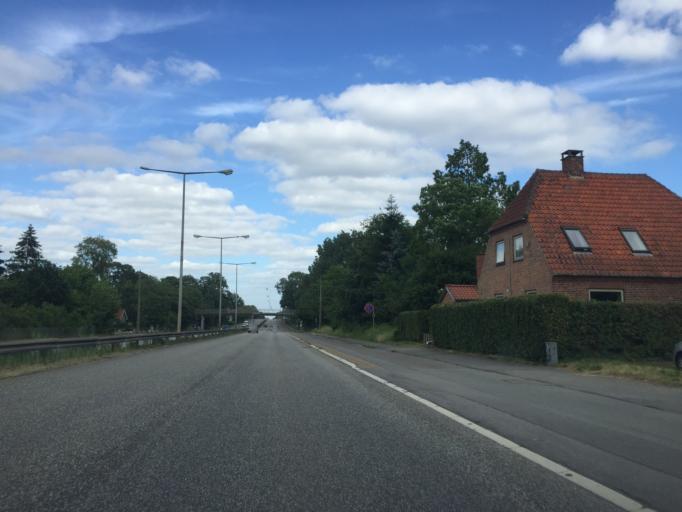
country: DK
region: Capital Region
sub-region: Hoje-Taastrup Kommune
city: Taastrup
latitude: 55.6596
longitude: 12.3197
